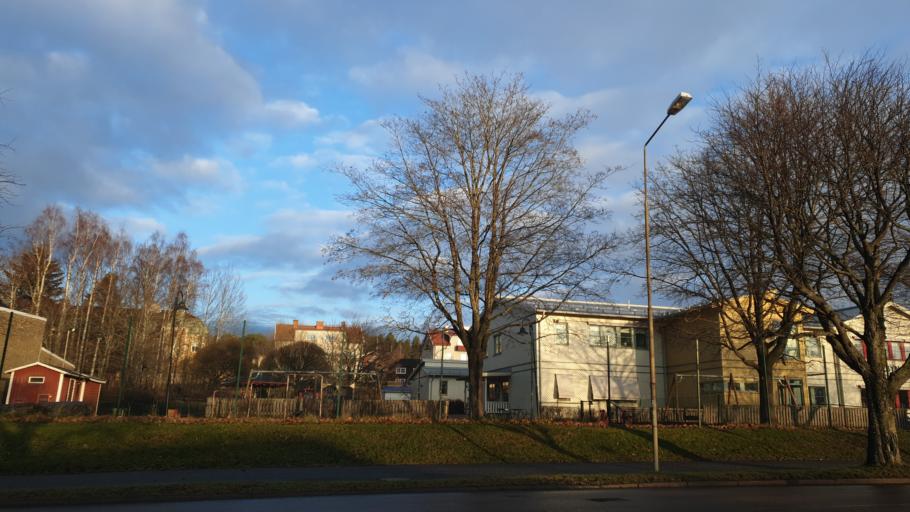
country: SE
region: Gaevleborg
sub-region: Hudiksvalls Kommun
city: Hudiksvall
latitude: 61.7258
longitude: 17.1252
